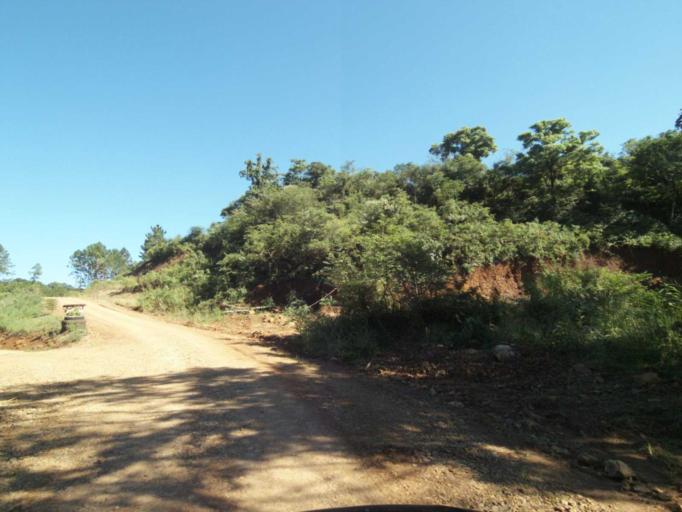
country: BR
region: Parana
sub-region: Francisco Beltrao
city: Francisco Beltrao
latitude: -26.1423
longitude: -53.3170
